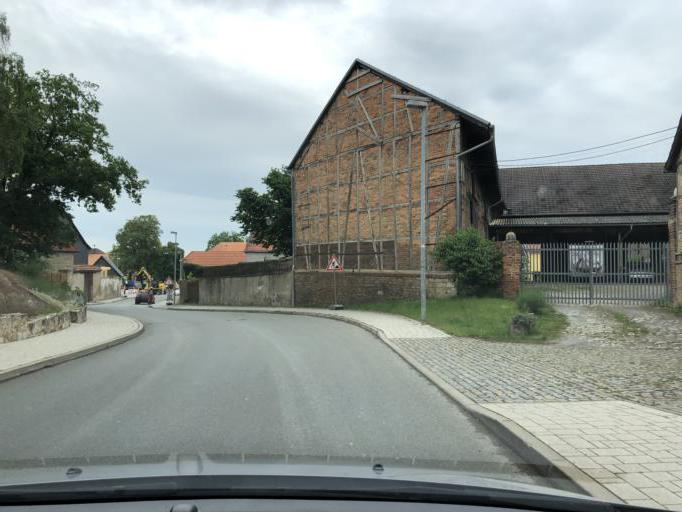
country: DE
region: Thuringia
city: Ossmanstedt
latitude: 51.0192
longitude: 11.4280
